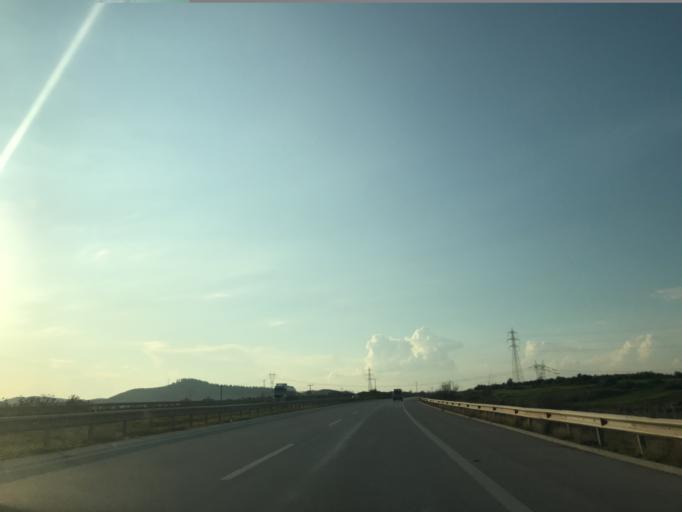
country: TR
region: Osmaniye
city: Toprakkale
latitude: 36.9676
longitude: 36.0369
